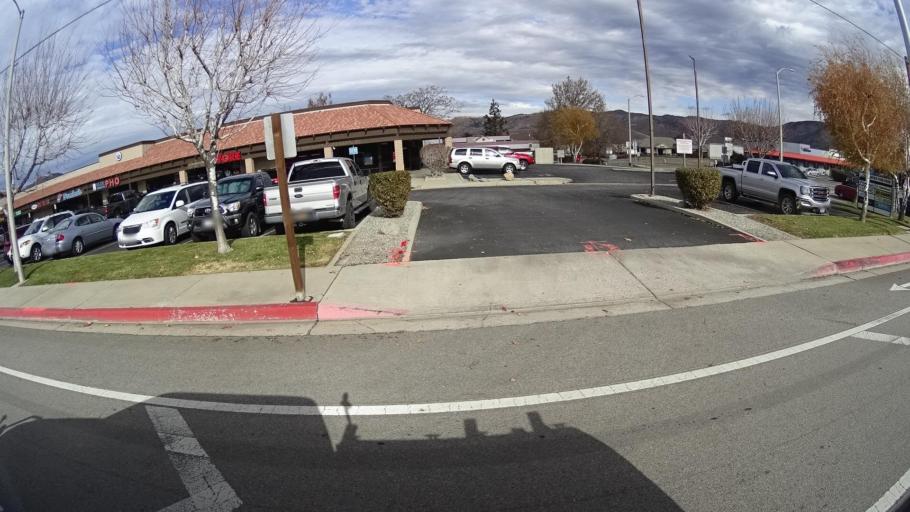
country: US
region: California
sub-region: Kern County
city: Tehachapi
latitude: 35.1244
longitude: -118.4681
